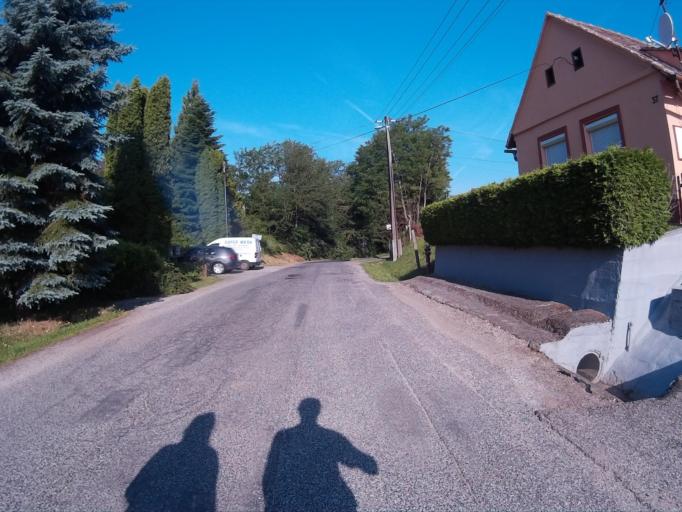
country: AT
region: Burgenland
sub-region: Politischer Bezirk Gussing
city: Heiligenbrunn
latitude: 46.9357
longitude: 16.4906
